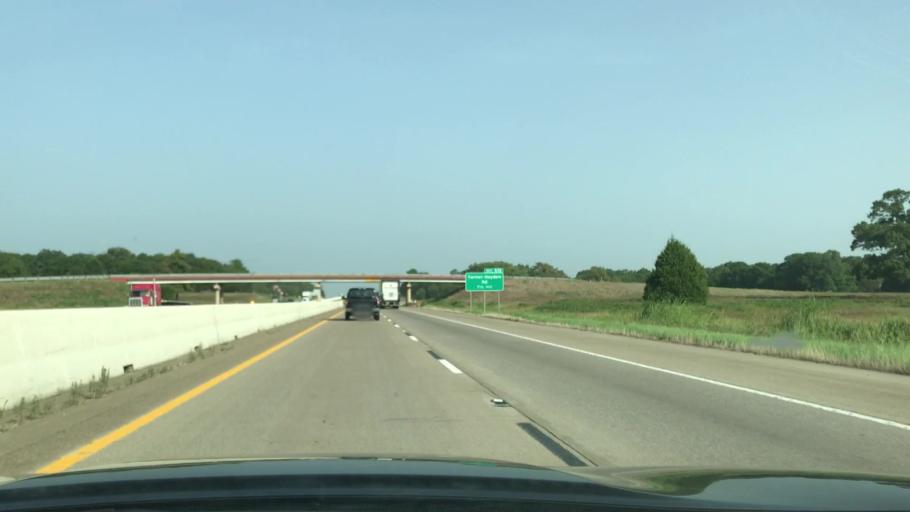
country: US
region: Texas
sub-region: Van Zandt County
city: Canton
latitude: 32.6071
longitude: -95.9490
